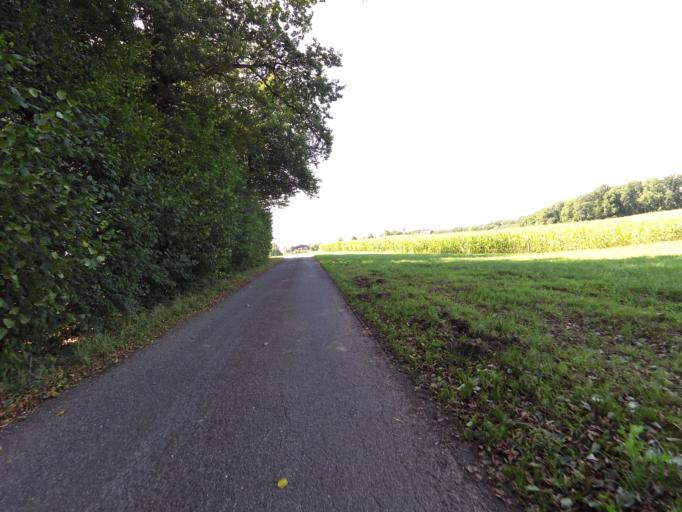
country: CH
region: Thurgau
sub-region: Kreuzlingen District
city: Tagerwilen
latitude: 47.6347
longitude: 9.1032
